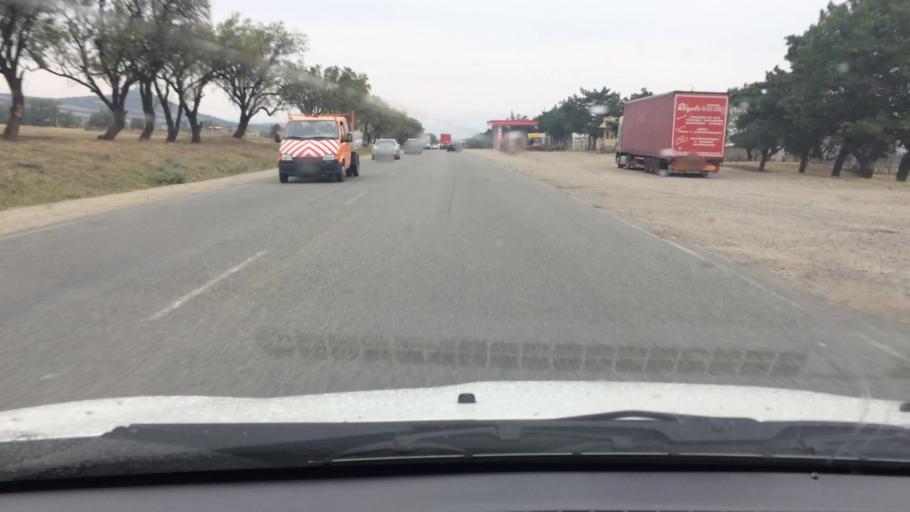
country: GE
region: T'bilisi
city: Tbilisi
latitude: 41.6333
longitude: 44.8170
